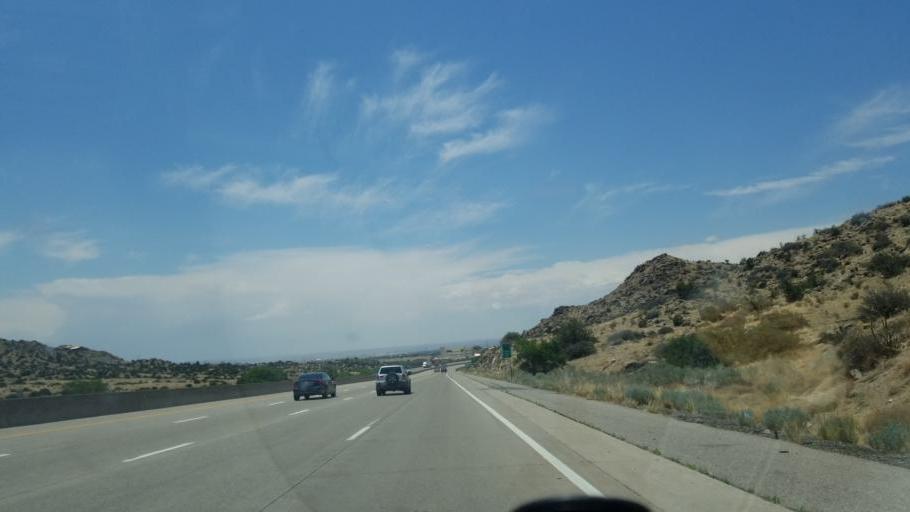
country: US
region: New Mexico
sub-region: Bernalillo County
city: Carnuel
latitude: 35.0632
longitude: -106.4733
